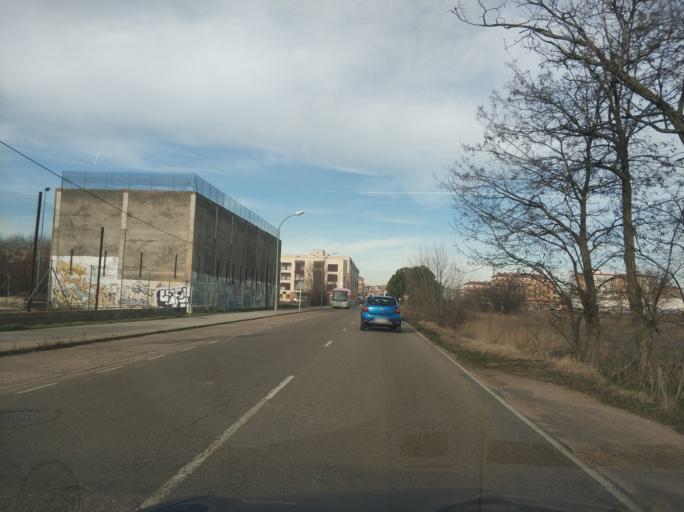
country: ES
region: Castille and Leon
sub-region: Provincia de Zamora
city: Zamora
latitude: 41.4937
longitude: -5.7383
